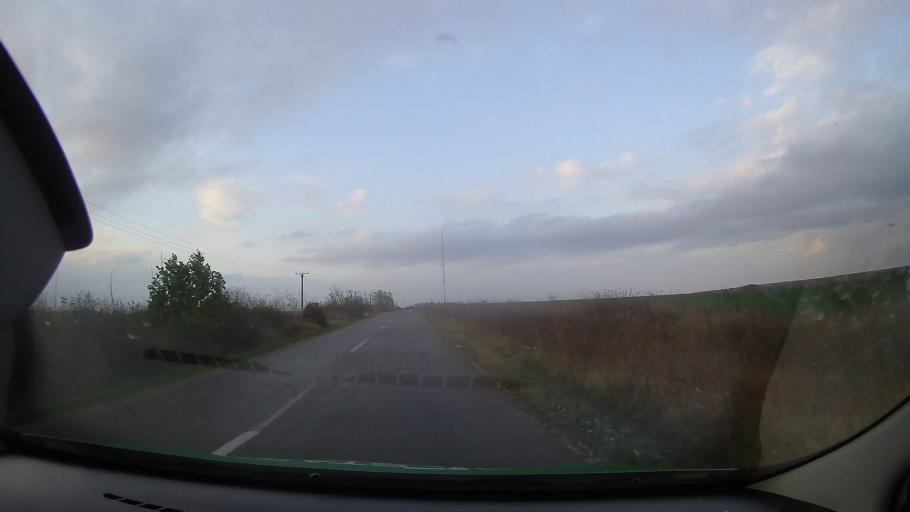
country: RO
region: Constanta
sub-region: Comuna Dobromir
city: Dobromir
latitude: 44.0407
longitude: 27.7567
